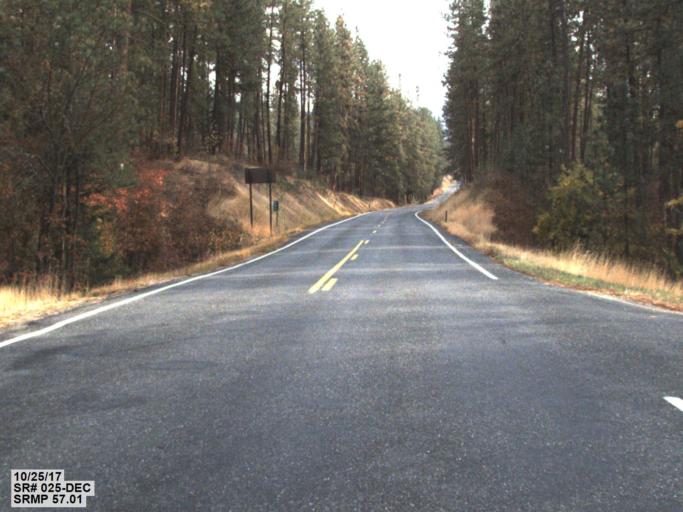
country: US
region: Washington
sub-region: Stevens County
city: Kettle Falls
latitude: 48.2975
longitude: -118.1455
